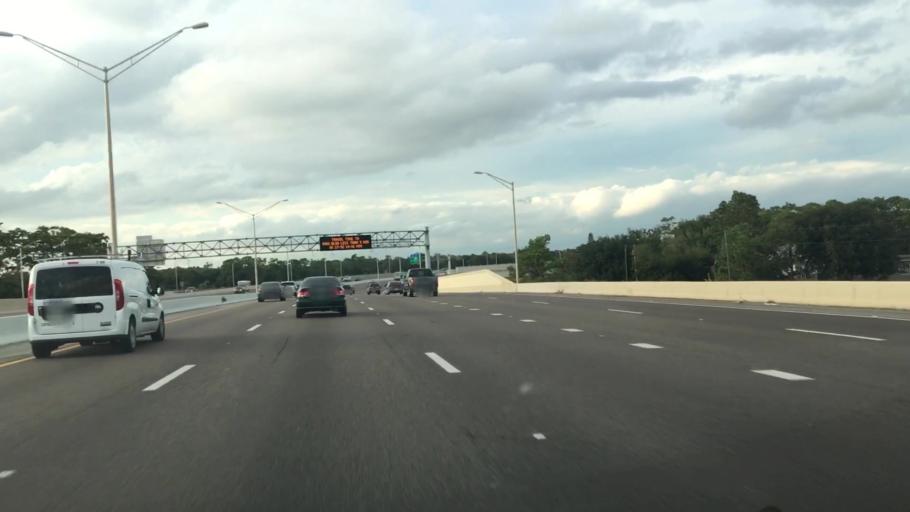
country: US
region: Florida
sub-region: Orange County
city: Union Park
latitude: 28.5544
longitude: -81.2654
